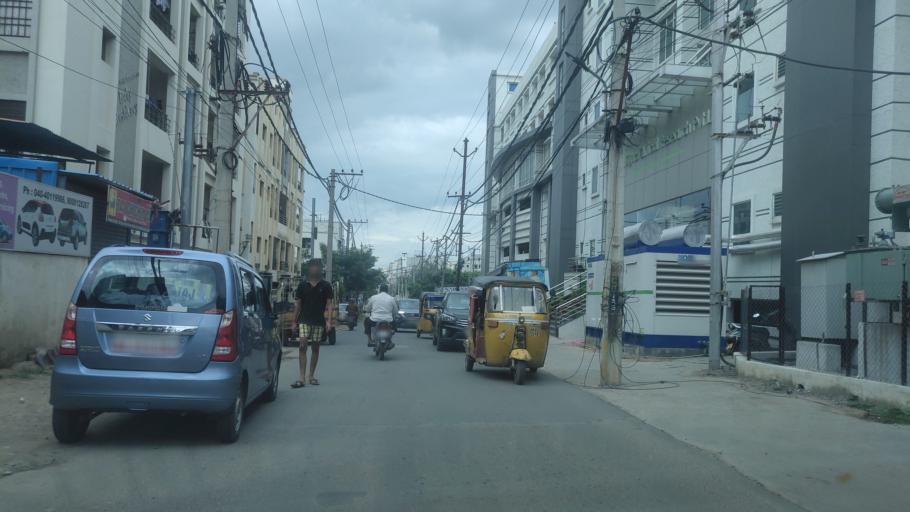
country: IN
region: Telangana
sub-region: Medak
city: Serilingampalle
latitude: 17.4951
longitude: 78.3482
